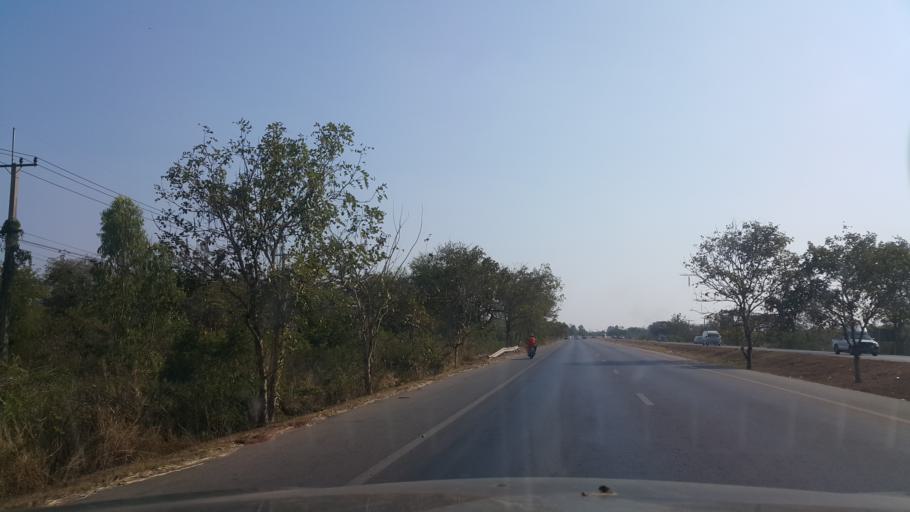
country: TH
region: Khon Kaen
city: Khon Kaen
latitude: 16.4279
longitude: 102.9175
